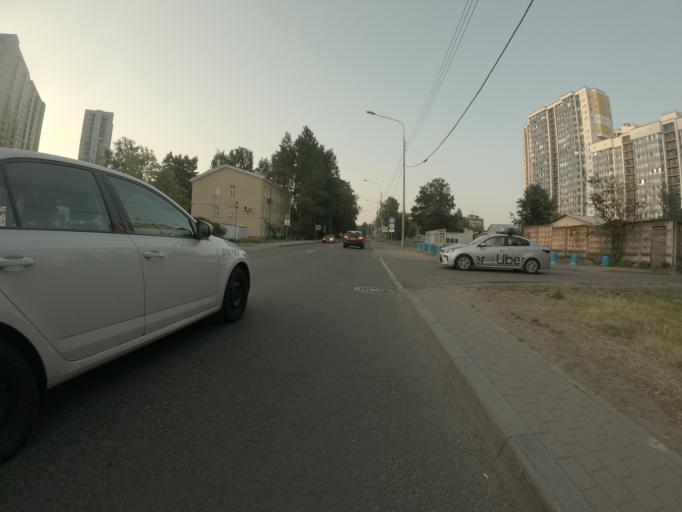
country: RU
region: Leningrad
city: Kalininskiy
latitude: 59.9846
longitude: 30.3897
